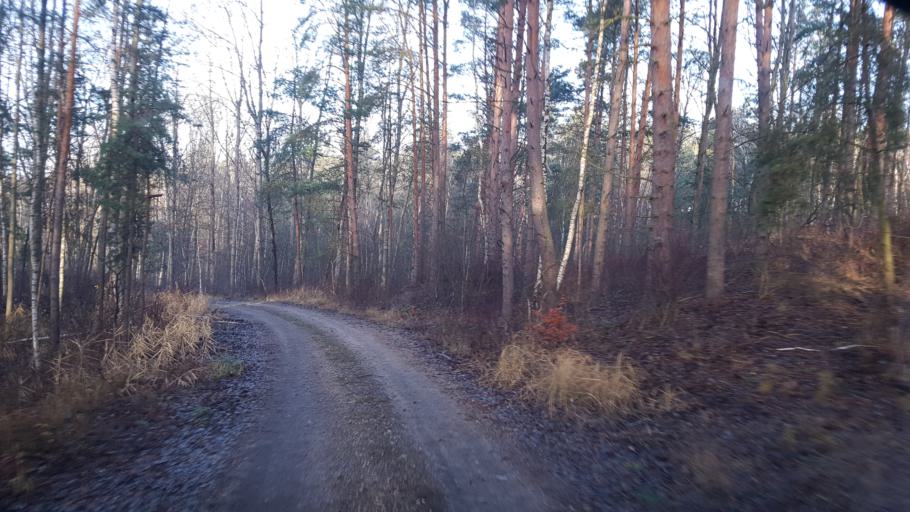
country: DE
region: Brandenburg
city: Trobitz
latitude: 51.5868
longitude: 13.4419
